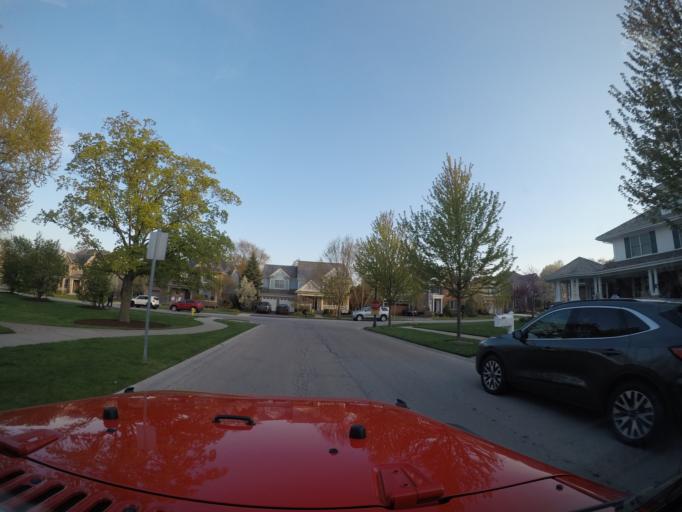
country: US
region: Illinois
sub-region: Cook County
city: Glenview
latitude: 42.0810
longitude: -87.8312
